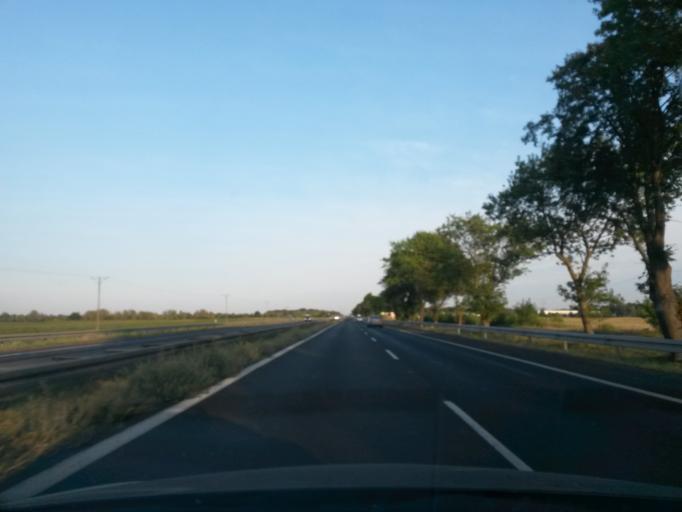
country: PL
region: Masovian Voivodeship
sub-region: Powiat warszawski zachodni
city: Dziekanow Lesny
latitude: 52.3695
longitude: 20.7980
